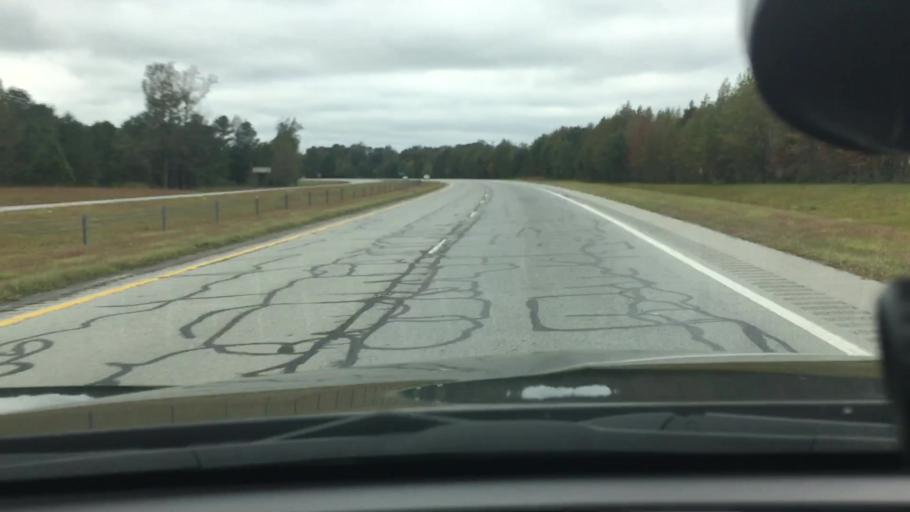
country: US
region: North Carolina
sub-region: Pitt County
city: Farmville
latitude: 35.6183
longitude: -77.5885
